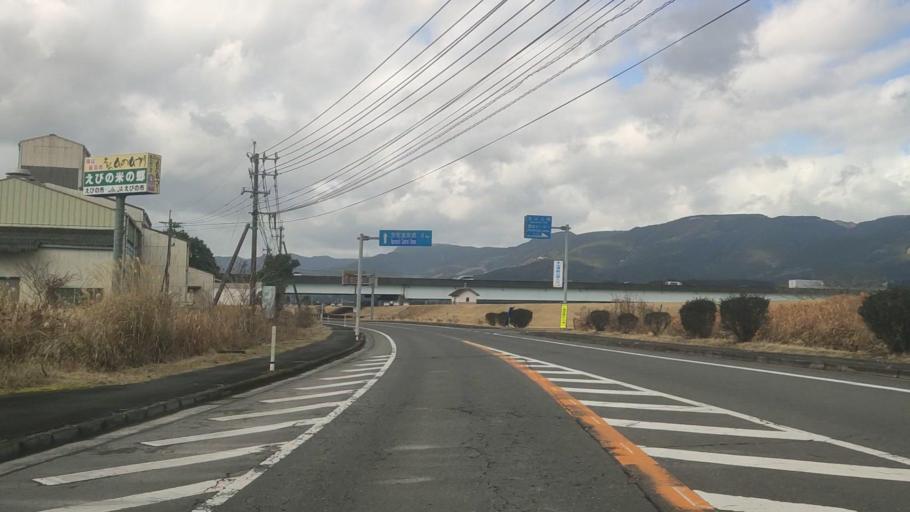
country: JP
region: Kumamoto
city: Hitoyoshi
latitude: 32.0525
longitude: 130.8036
